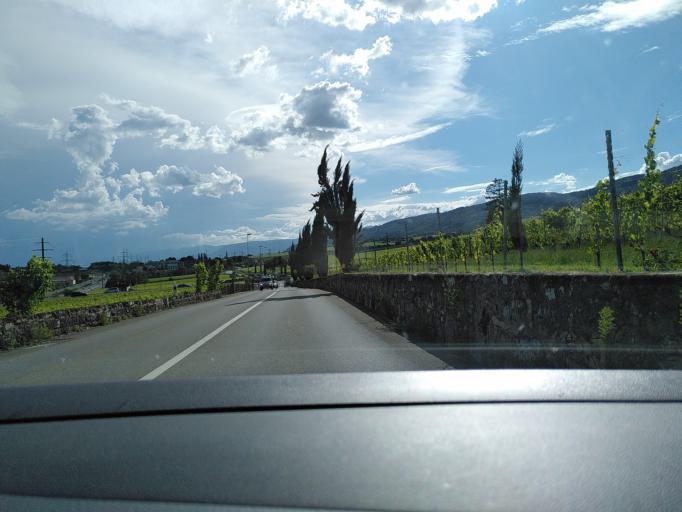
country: CH
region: Vaud
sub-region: Nyon District
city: Rolle
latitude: 46.4669
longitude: 6.3343
